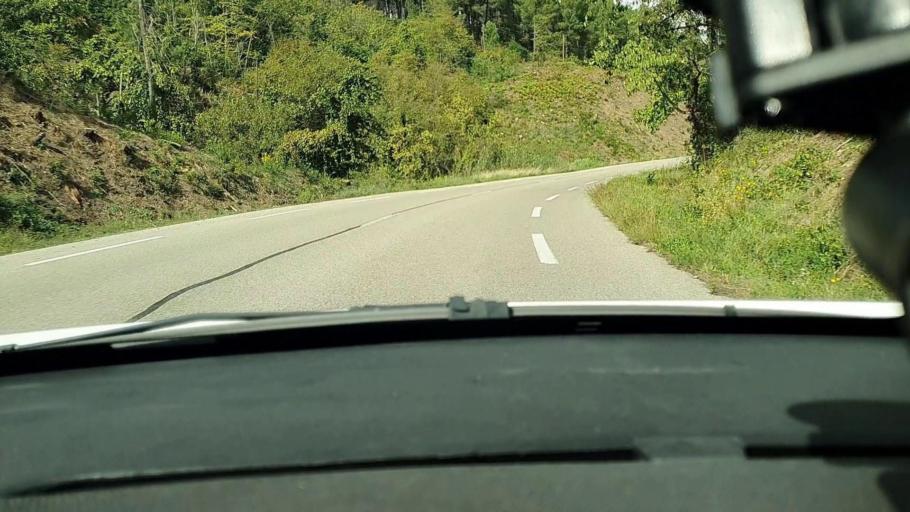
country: FR
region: Languedoc-Roussillon
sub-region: Departement du Gard
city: Laval-Pradel
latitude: 44.2319
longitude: 4.0541
